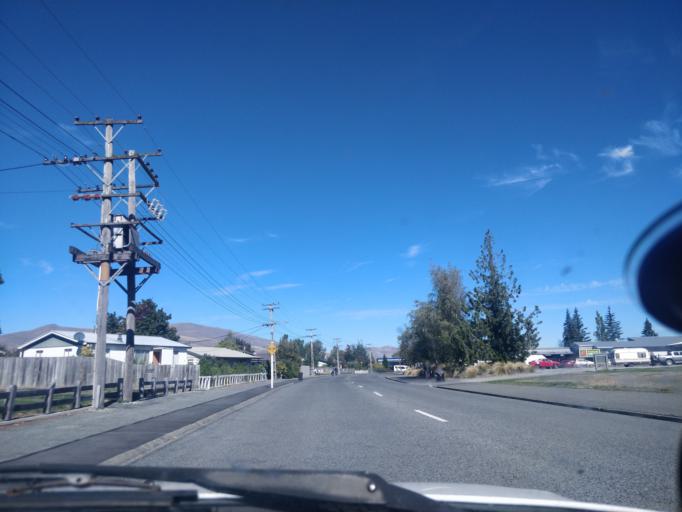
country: NZ
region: Canterbury
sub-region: Timaru District
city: Pleasant Point
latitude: -44.2557
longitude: 170.1012
